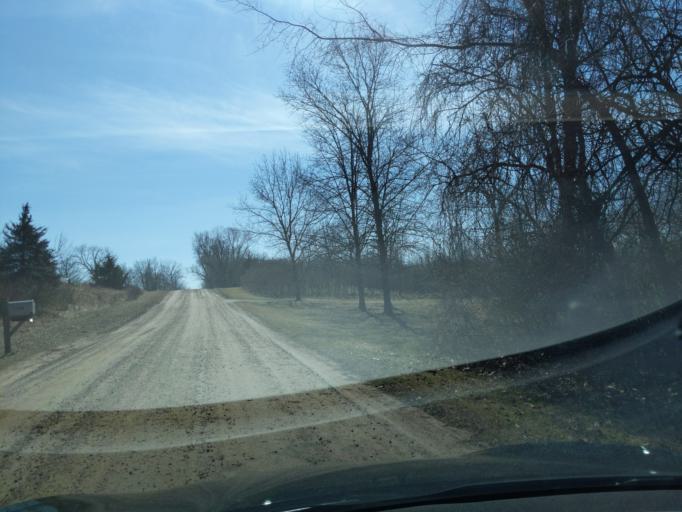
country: US
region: Michigan
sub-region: Ionia County
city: Lake Odessa
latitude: 42.7263
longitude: -85.0539
